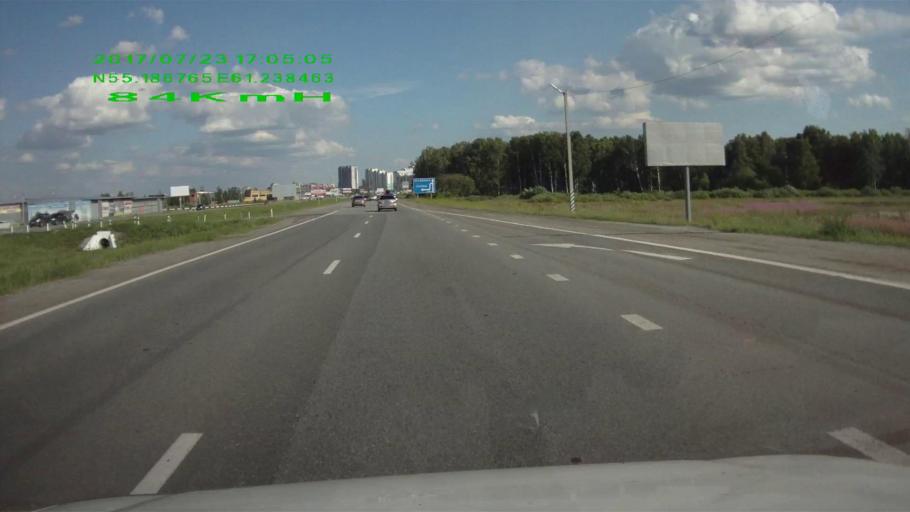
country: RU
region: Chelyabinsk
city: Roshchino
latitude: 55.1861
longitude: 61.2397
